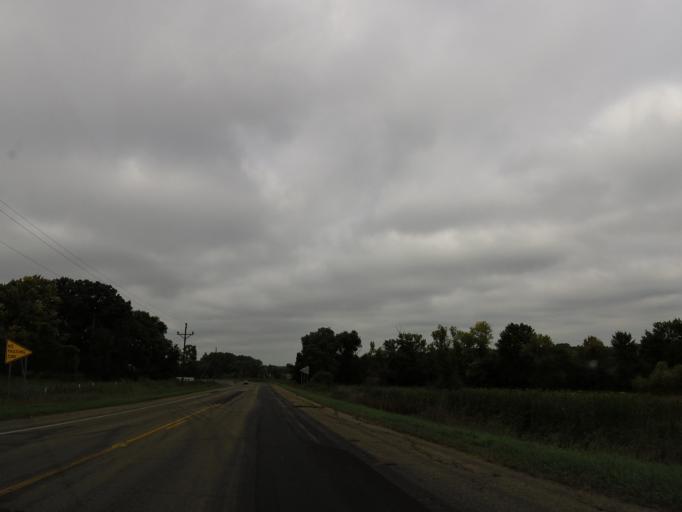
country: US
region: Minnesota
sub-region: Yellow Medicine County
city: Granite Falls
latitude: 44.8496
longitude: -95.6190
